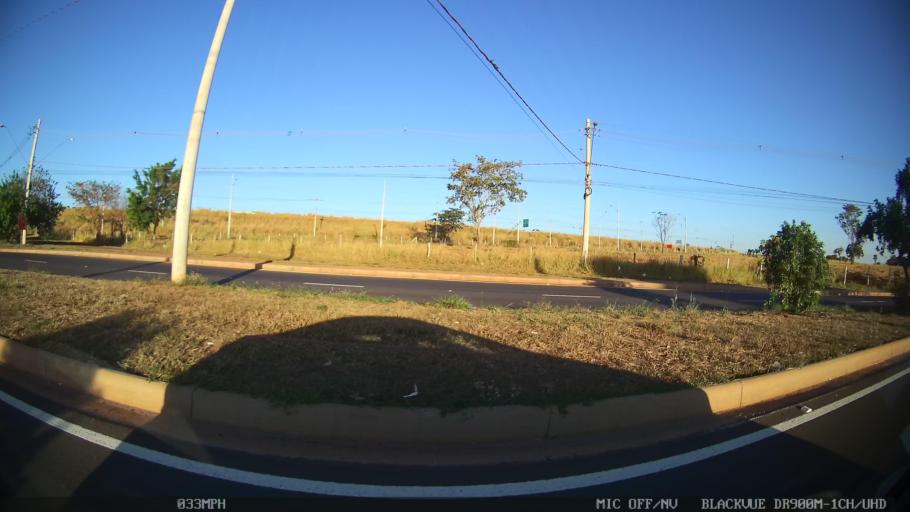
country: BR
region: Sao Paulo
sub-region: Sao Jose Do Rio Preto
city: Sao Jose do Rio Preto
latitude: -20.7629
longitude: -49.3484
